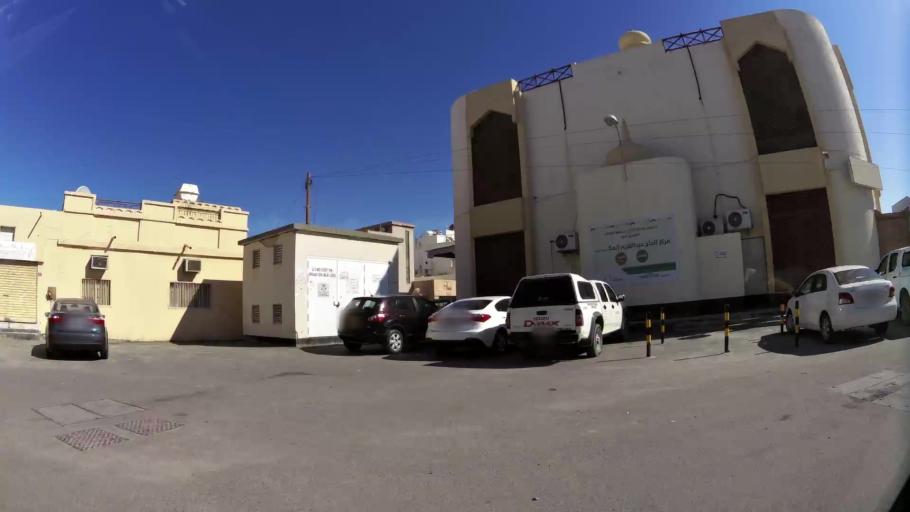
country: BH
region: Muharraq
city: Al Muharraq
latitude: 26.2651
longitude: 50.6183
